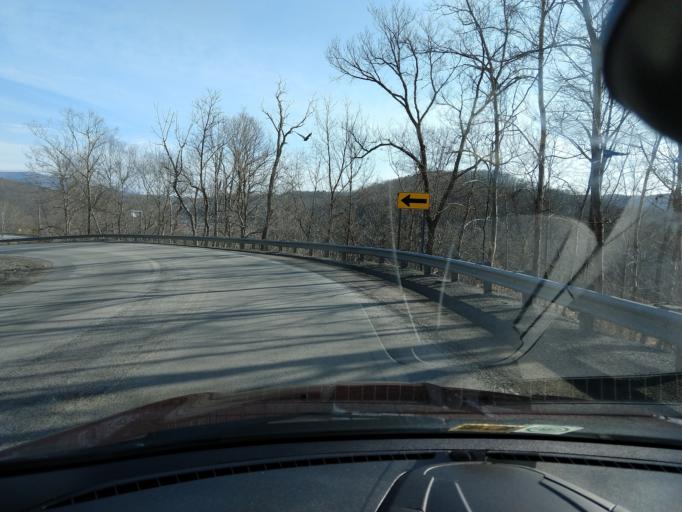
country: US
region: West Virginia
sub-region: Pocahontas County
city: Marlinton
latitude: 38.2131
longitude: -80.1029
